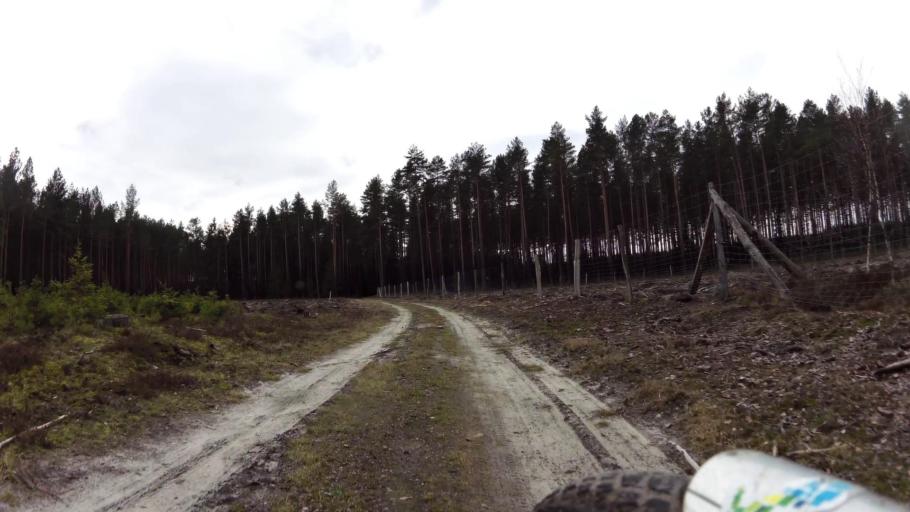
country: PL
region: Pomeranian Voivodeship
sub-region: Powiat bytowski
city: Kolczyglowy
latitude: 54.1584
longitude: 17.1893
